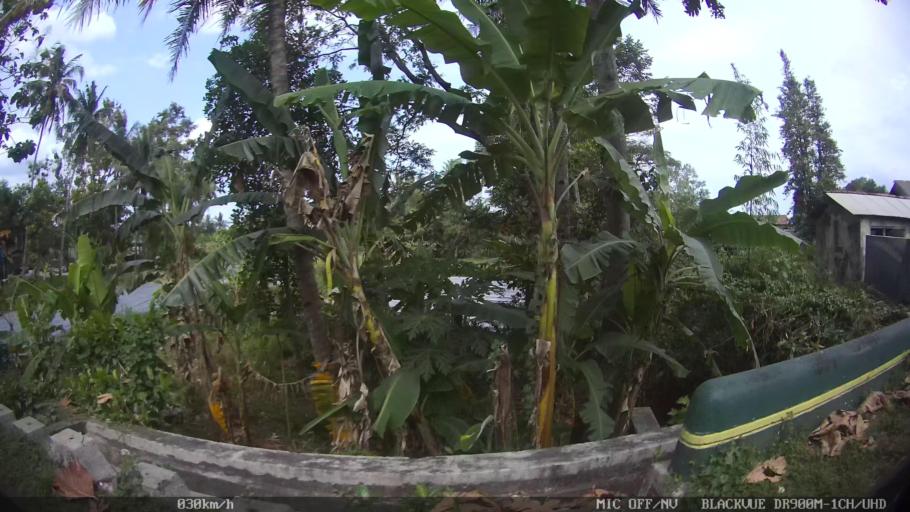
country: ID
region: Central Java
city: Candi Prambanan
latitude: -7.7292
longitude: 110.4686
